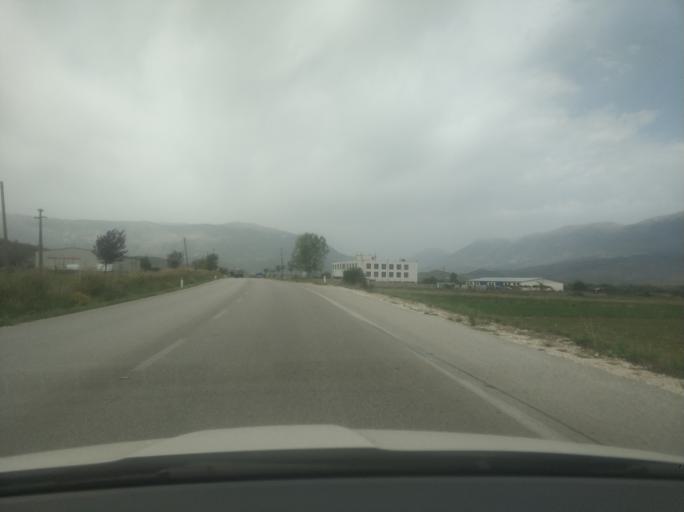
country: AL
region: Gjirokaster
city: Gjirokaster
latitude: 40.1167
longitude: 20.1179
